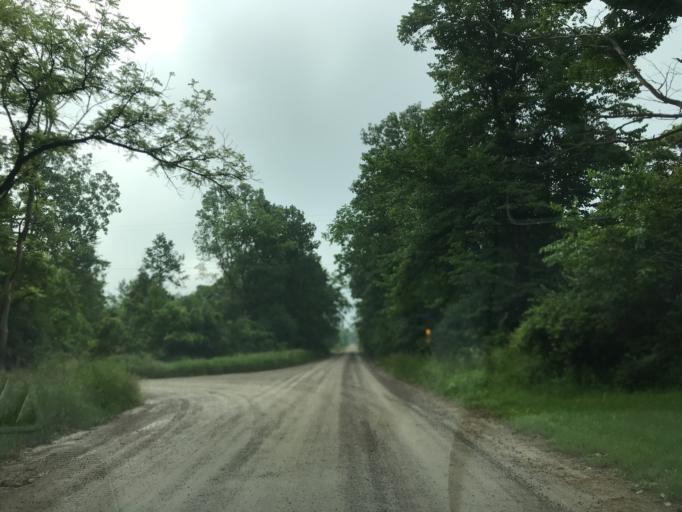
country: US
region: Michigan
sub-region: Washtenaw County
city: Ypsilanti
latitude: 42.2897
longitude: -83.6192
